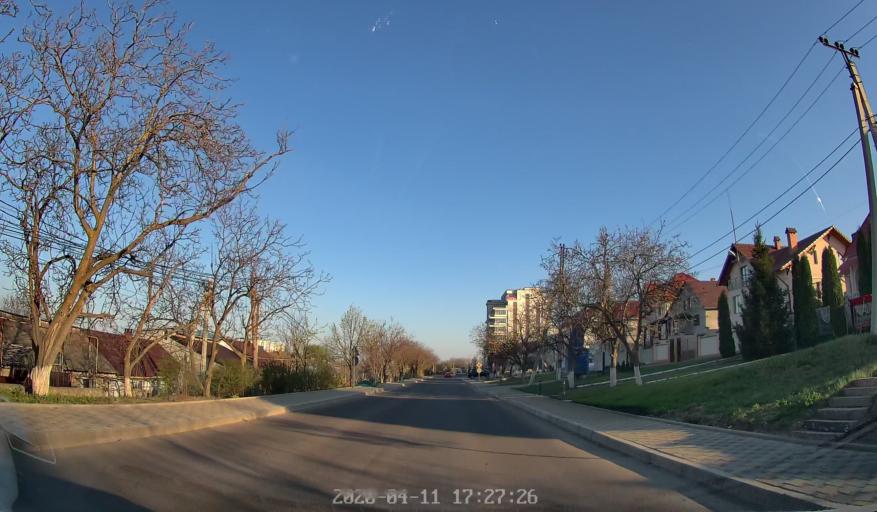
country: MD
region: Laloveni
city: Ialoveni
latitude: 47.0087
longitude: 28.7628
